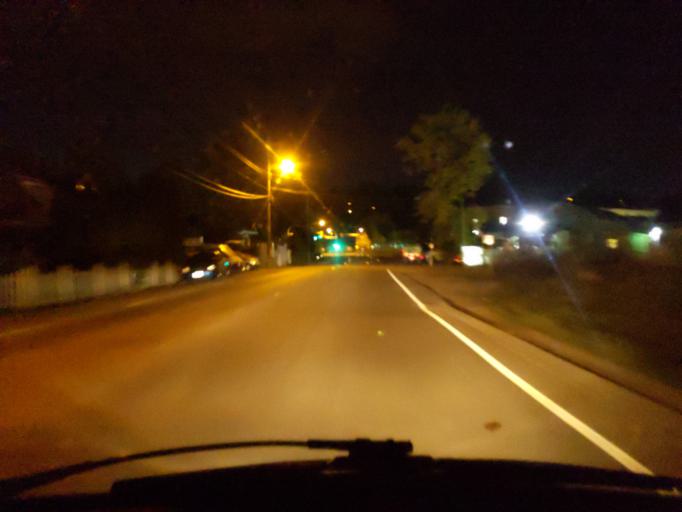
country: CA
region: British Columbia
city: New Westminster
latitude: 49.1985
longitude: -122.8810
